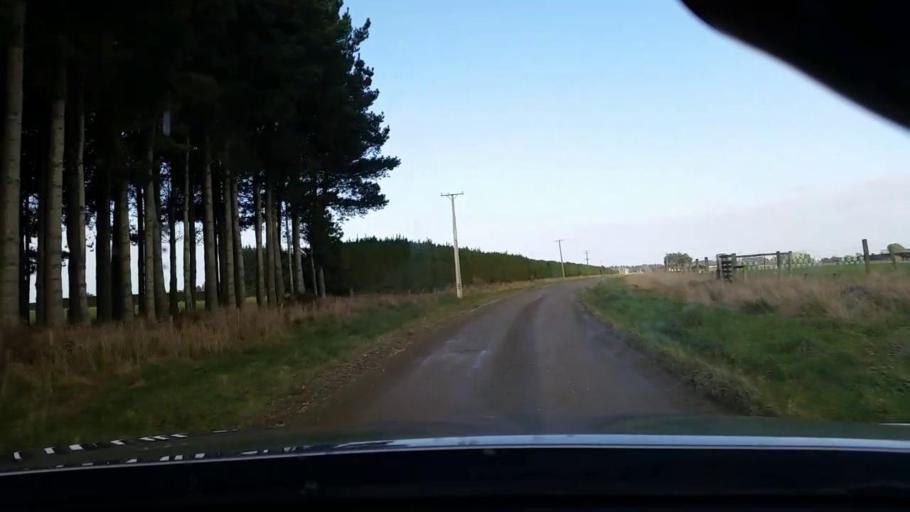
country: NZ
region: Southland
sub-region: Invercargill City
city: Invercargill
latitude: -46.2823
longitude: 168.2945
